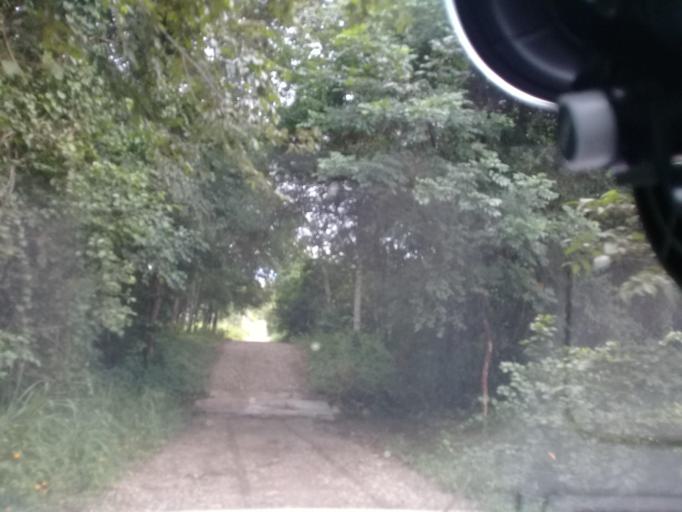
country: MX
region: Hidalgo
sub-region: Huejutla de Reyes
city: Chalahuiyapa
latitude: 21.1688
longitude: -98.3702
